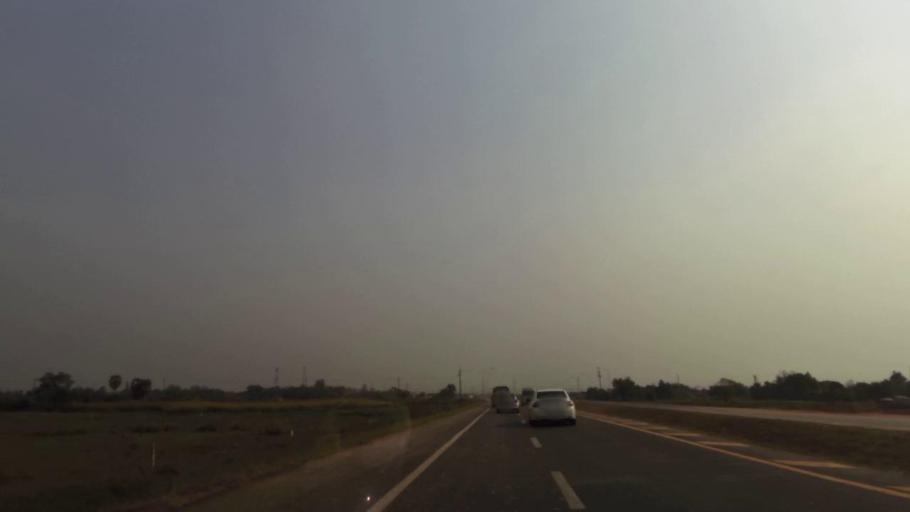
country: TH
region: Rayong
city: Klaeng
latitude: 12.7900
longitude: 101.6753
